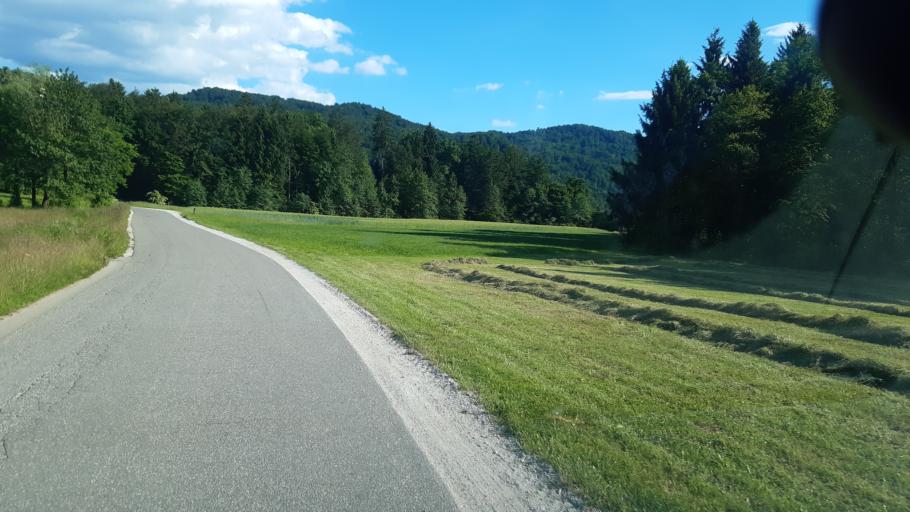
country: SI
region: Vodice
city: Vodice
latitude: 46.1672
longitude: 14.5152
